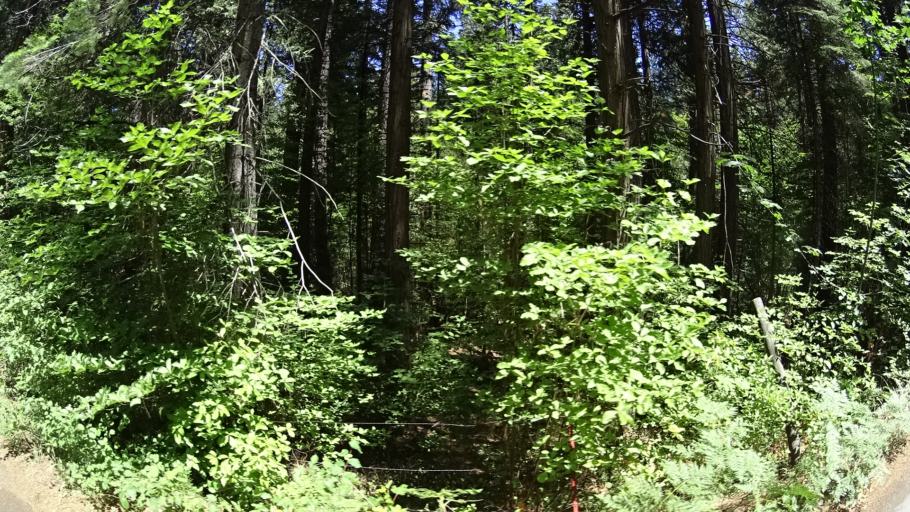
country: US
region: California
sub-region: Calaveras County
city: Arnold
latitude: 38.2202
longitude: -120.3584
